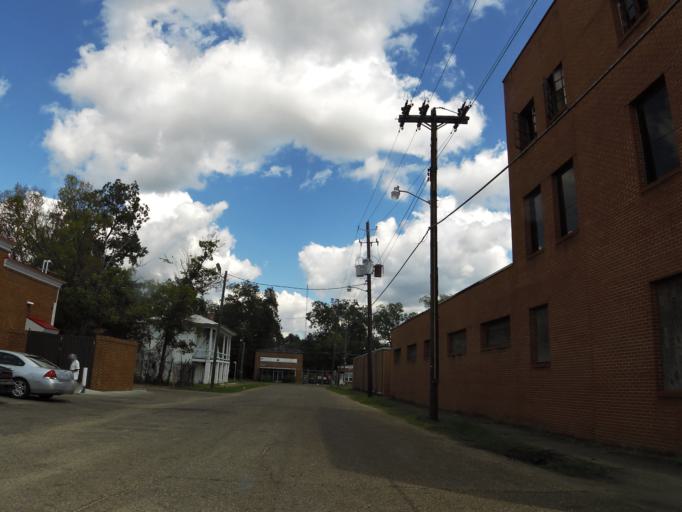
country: US
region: Alabama
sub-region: Dallas County
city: Selma
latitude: 32.4135
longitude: -87.0230
